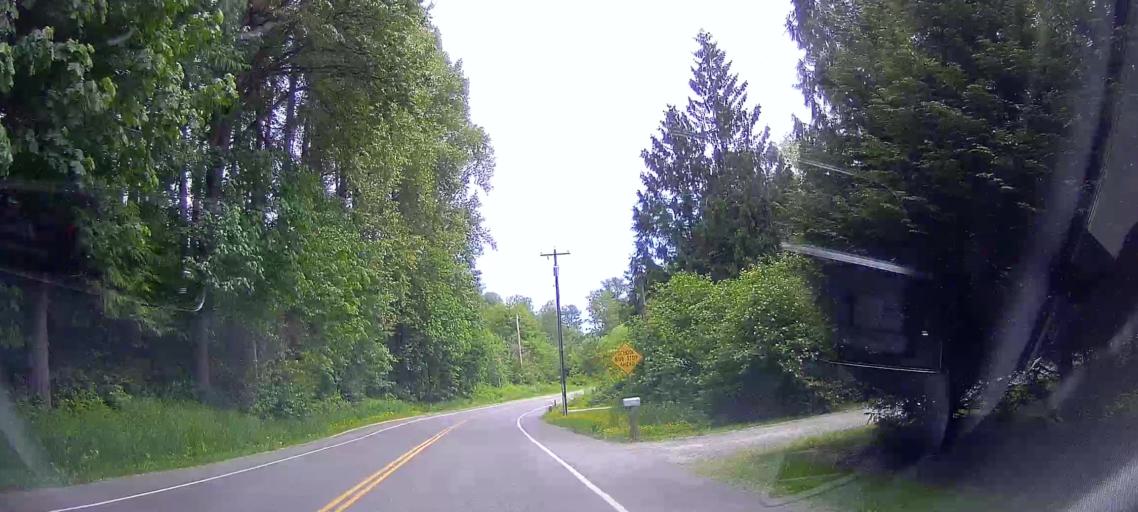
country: US
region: Washington
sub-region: Snohomish County
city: Bryant
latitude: 48.2387
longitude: -122.2080
